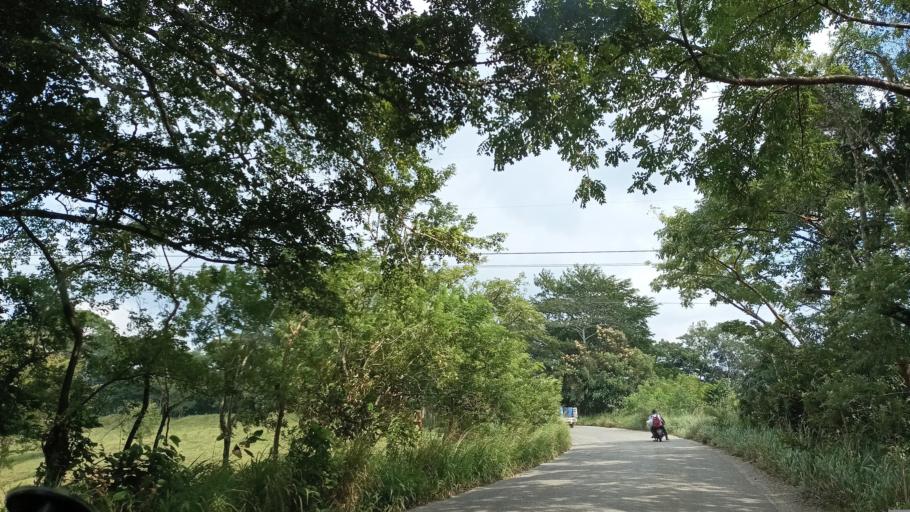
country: MX
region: Veracruz
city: Las Choapas
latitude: 17.7879
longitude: -94.1090
